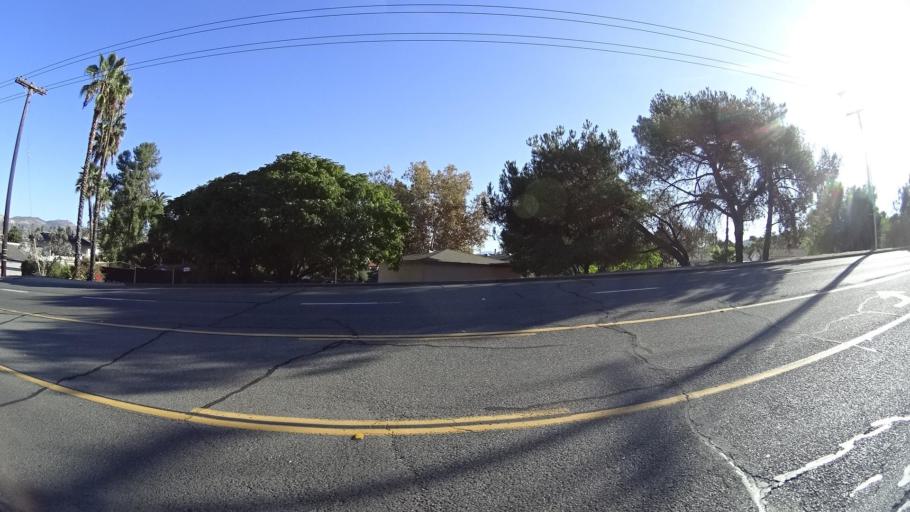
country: US
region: California
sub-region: San Diego County
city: Granite Hills
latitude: 32.8312
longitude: -116.9043
